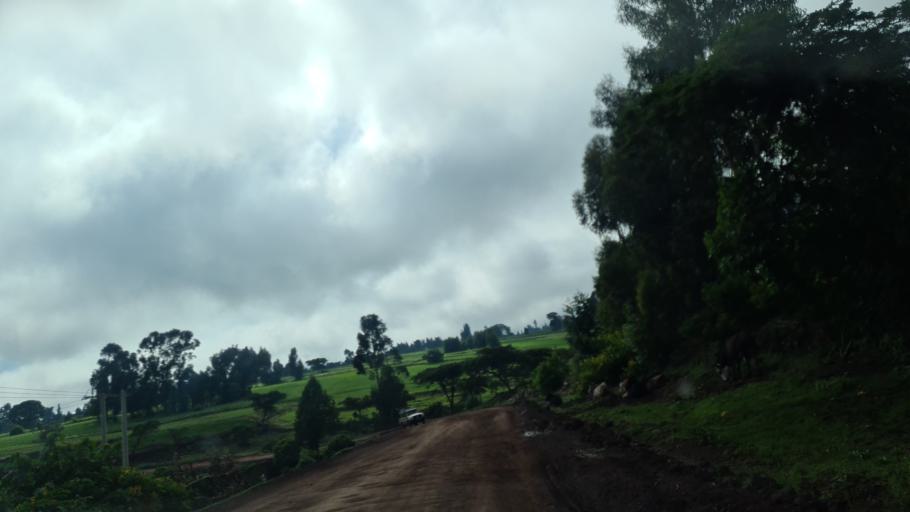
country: ET
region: Oromiya
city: Huruta
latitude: 8.1250
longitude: 39.3742
